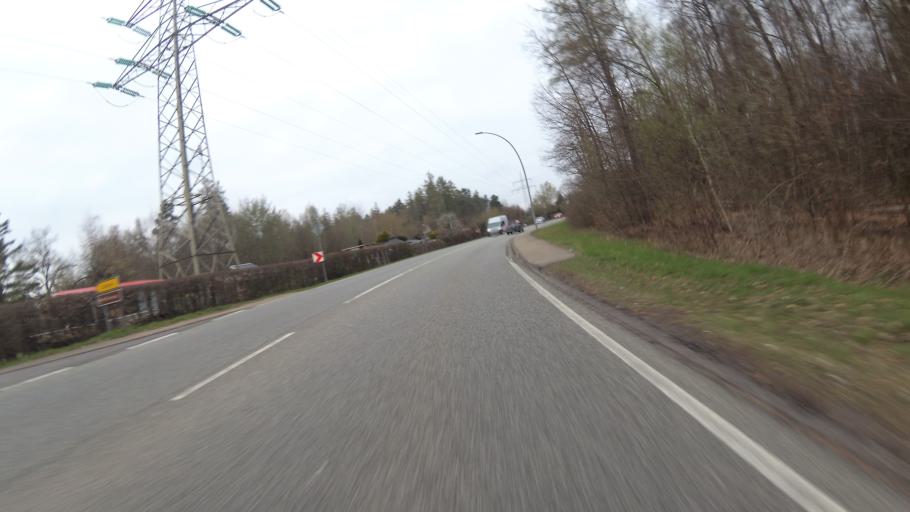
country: DE
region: Saarland
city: Sankt Ingbert
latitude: 49.2987
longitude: 7.1137
